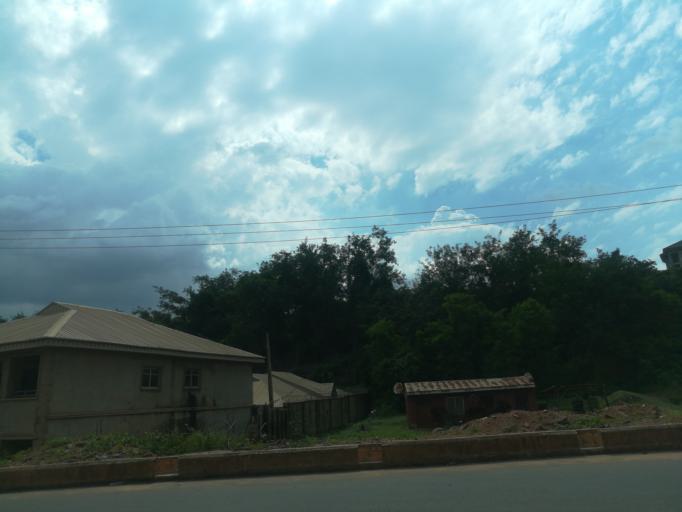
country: NG
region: Oyo
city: Ibadan
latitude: 7.4182
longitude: 3.8497
